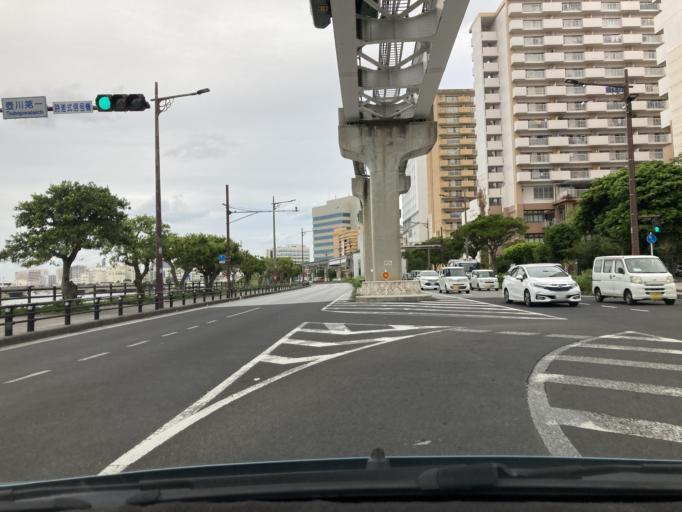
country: JP
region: Okinawa
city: Naha-shi
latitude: 26.2062
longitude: 127.6782
